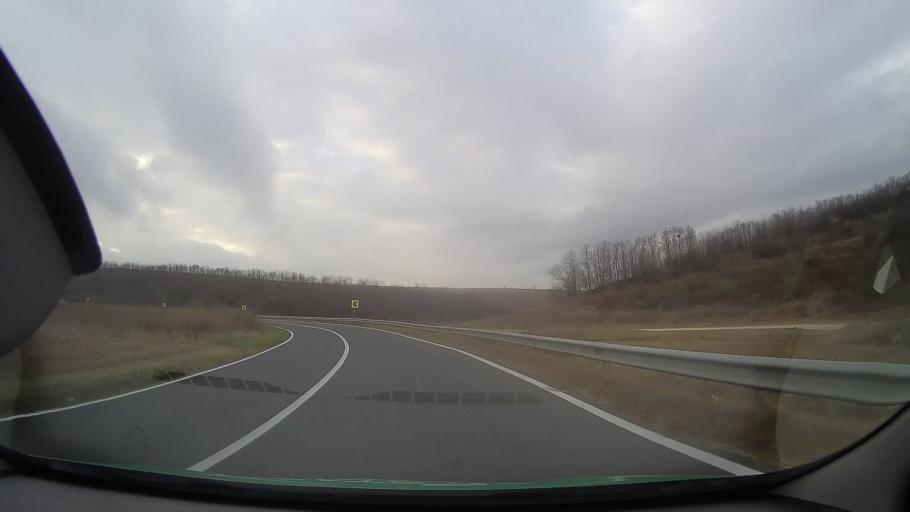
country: RO
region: Constanta
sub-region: Comuna Deleni
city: Deleni
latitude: 44.1024
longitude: 28.0263
